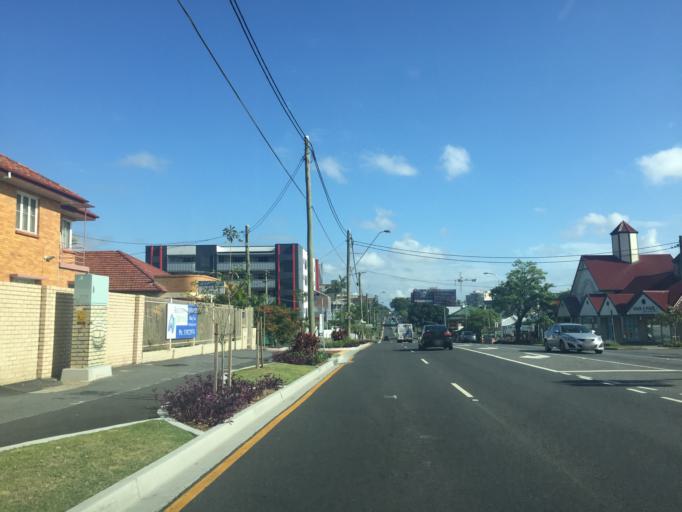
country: AU
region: Queensland
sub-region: Brisbane
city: Woolloongabba
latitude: -27.4828
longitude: 153.0358
